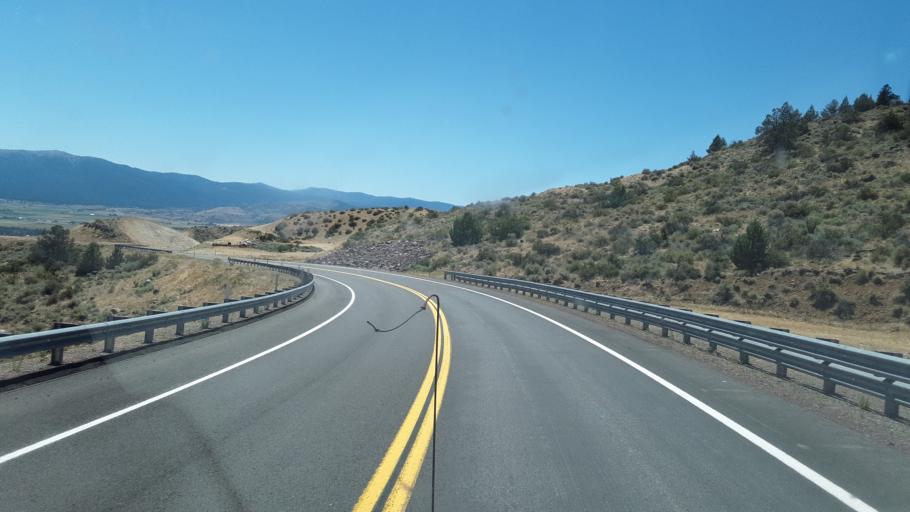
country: US
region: California
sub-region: Lassen County
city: Johnstonville
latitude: 40.4632
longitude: -120.5763
